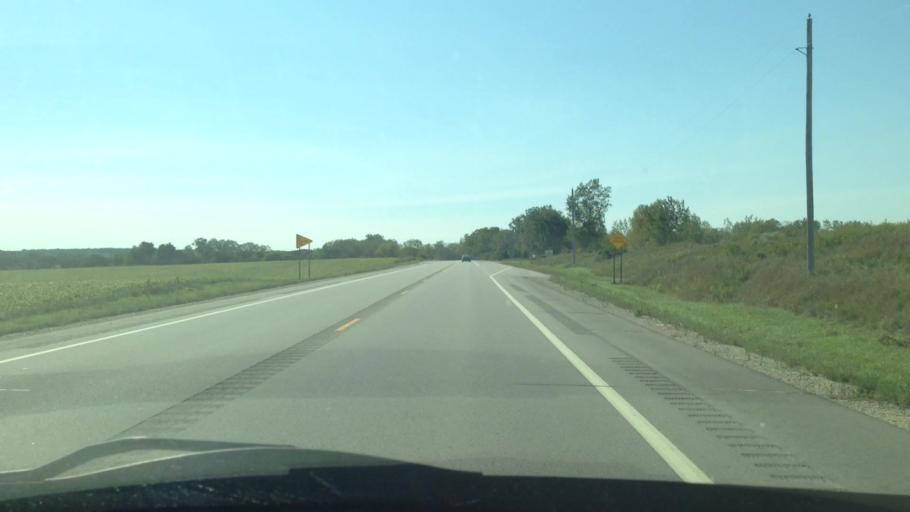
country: US
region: Minnesota
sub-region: Olmsted County
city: Eyota
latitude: 43.9994
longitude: -92.2829
